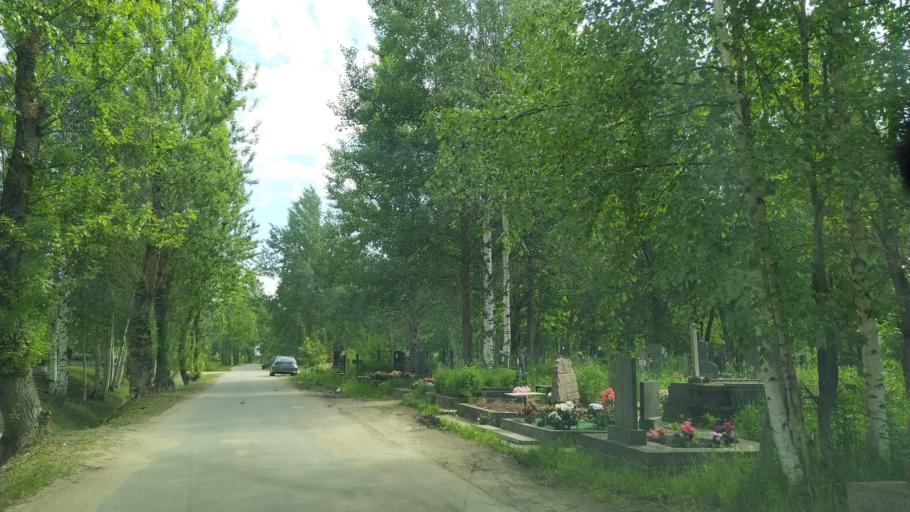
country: RU
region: St.-Petersburg
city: Dachnoye
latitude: 59.7726
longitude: 30.2693
